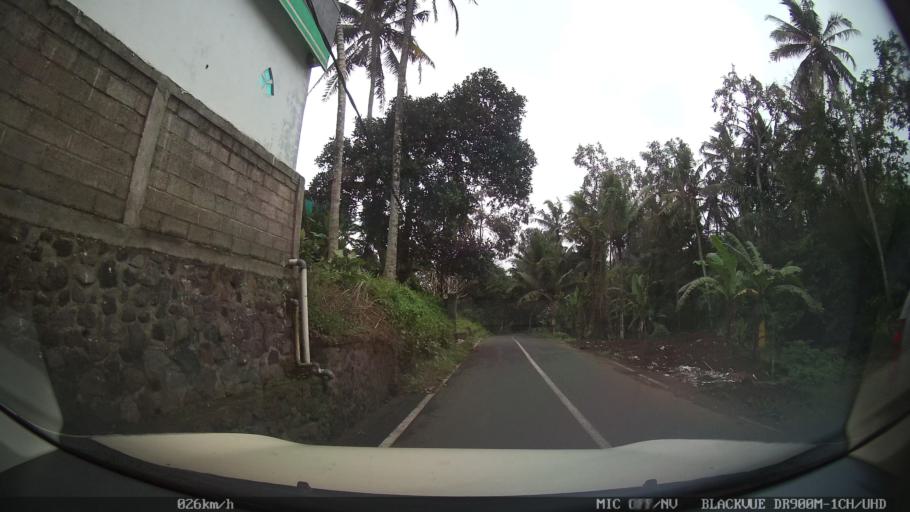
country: ID
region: Bali
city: Banjar Parekan
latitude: -8.5627
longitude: 115.2135
